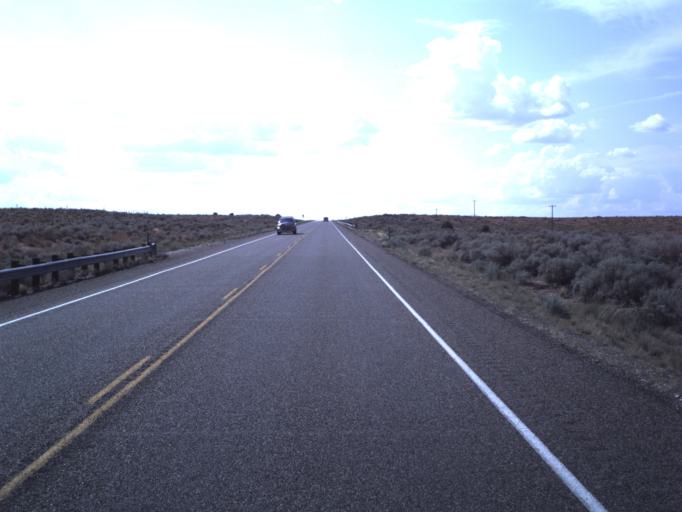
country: US
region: Arizona
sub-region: Coconino County
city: Page
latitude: 37.0881
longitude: -111.7046
